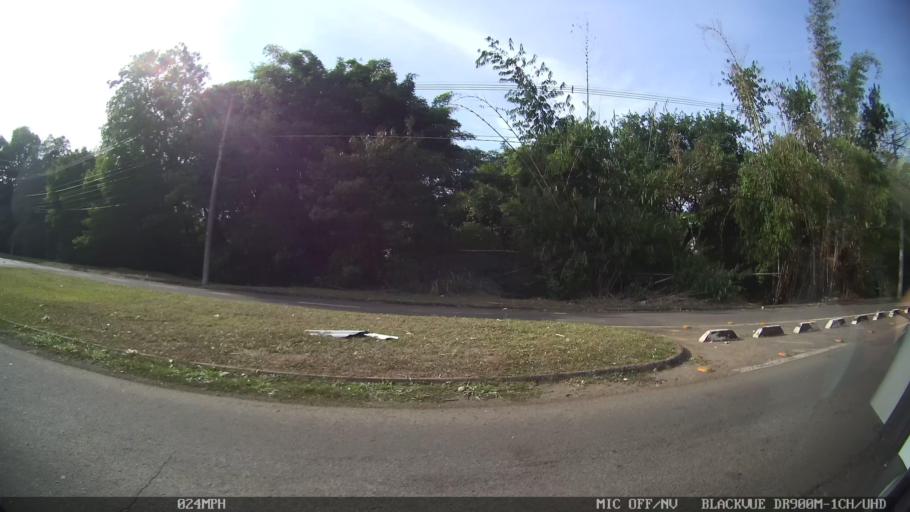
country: BR
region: Sao Paulo
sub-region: Piracicaba
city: Piracicaba
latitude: -22.7259
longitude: -47.6722
